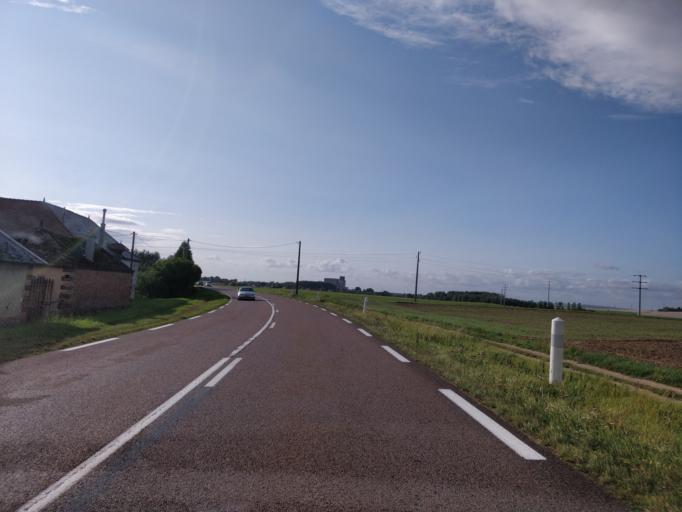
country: FR
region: Champagne-Ardenne
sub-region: Departement de l'Aube
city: Verrieres
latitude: 48.2795
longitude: 4.1954
